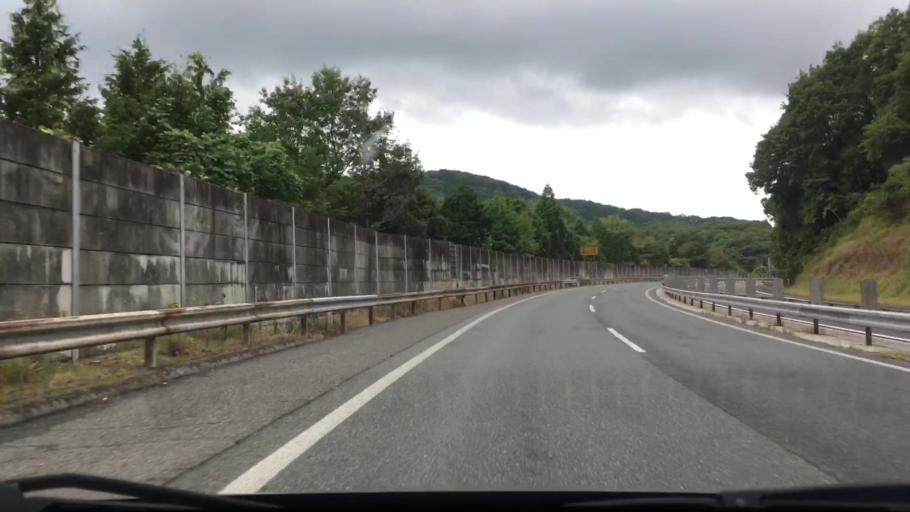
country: JP
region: Okayama
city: Niimi
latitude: 34.9034
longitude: 133.3017
